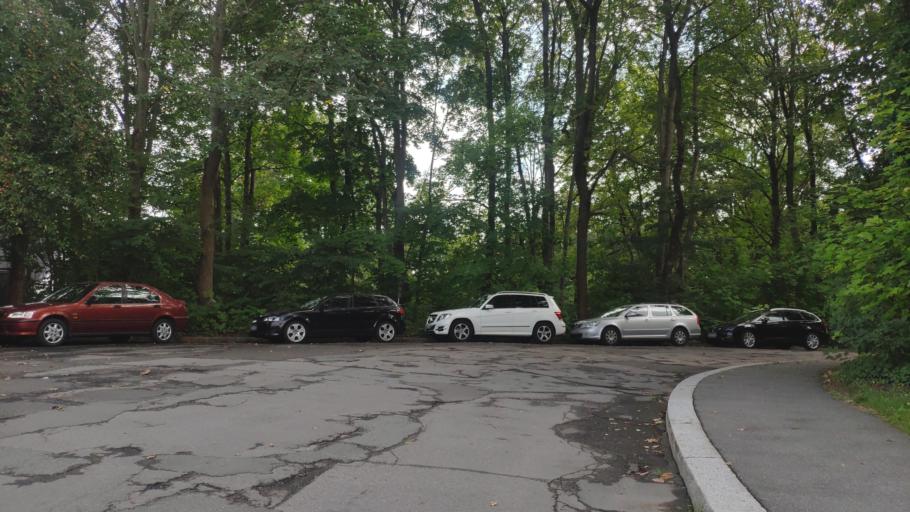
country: DE
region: Saxony
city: Chemnitz
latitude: 50.8246
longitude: 12.9152
